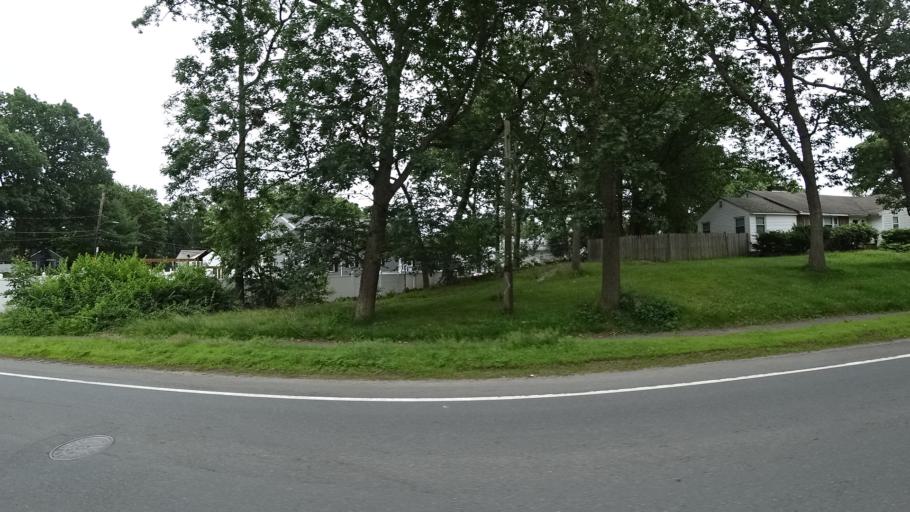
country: US
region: Massachusetts
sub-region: Norfolk County
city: Dedham
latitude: 42.2290
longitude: -71.1515
